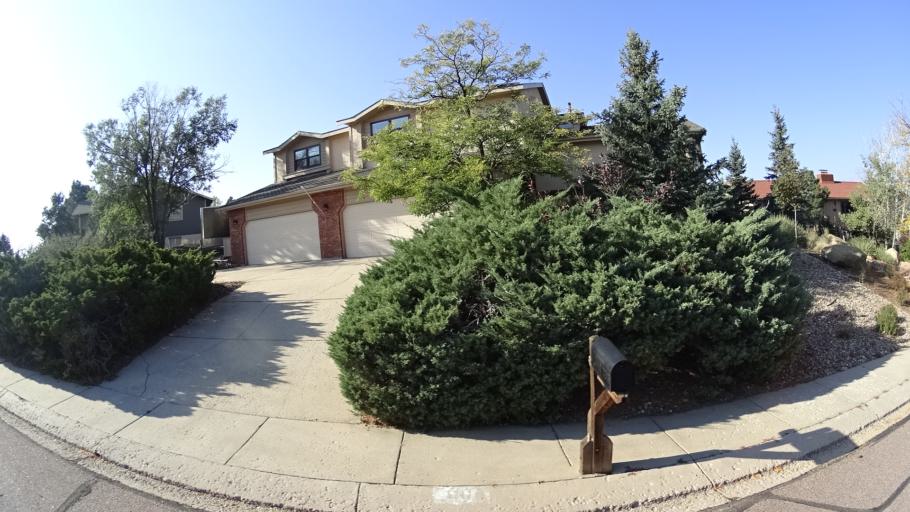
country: US
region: Colorado
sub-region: El Paso County
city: Cimarron Hills
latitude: 38.8935
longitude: -104.7286
